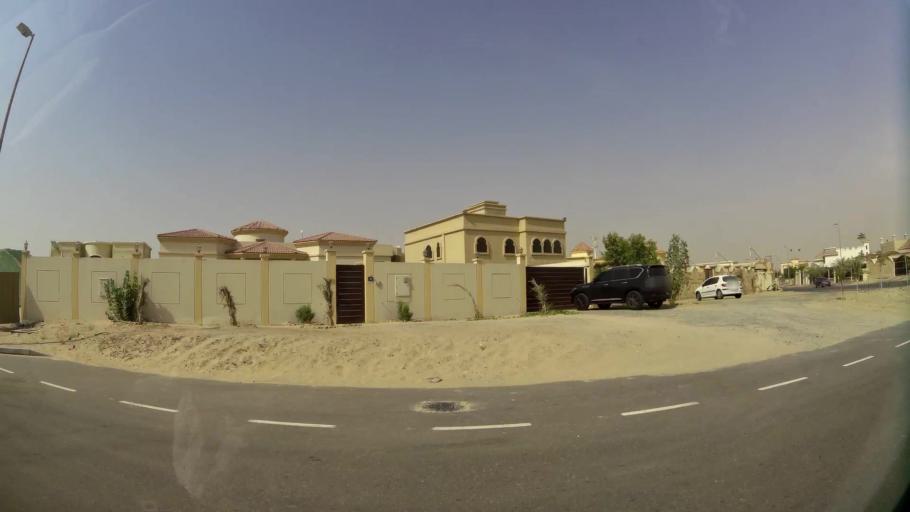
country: AE
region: Ash Shariqah
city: Sharjah
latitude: 25.2644
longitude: 55.4666
